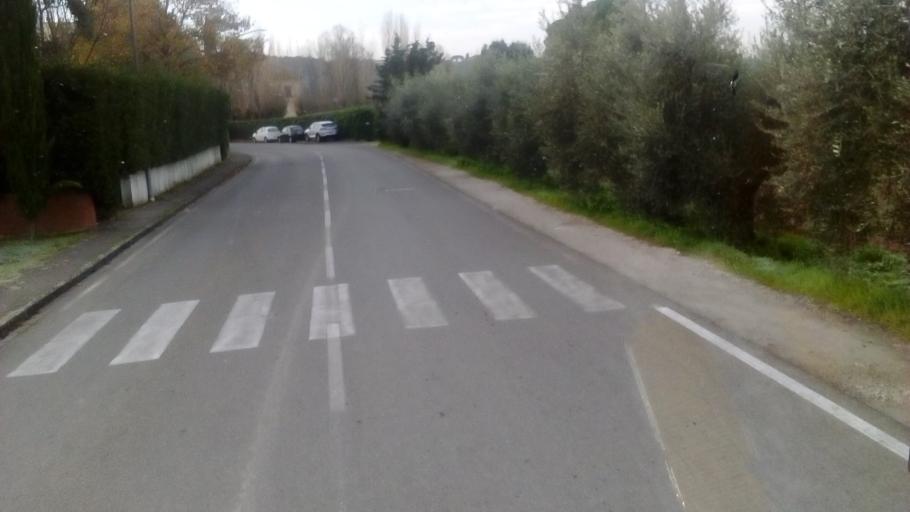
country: IT
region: Tuscany
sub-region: Province of Florence
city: Montelupo Fiorentino
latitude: 43.7063
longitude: 10.9896
